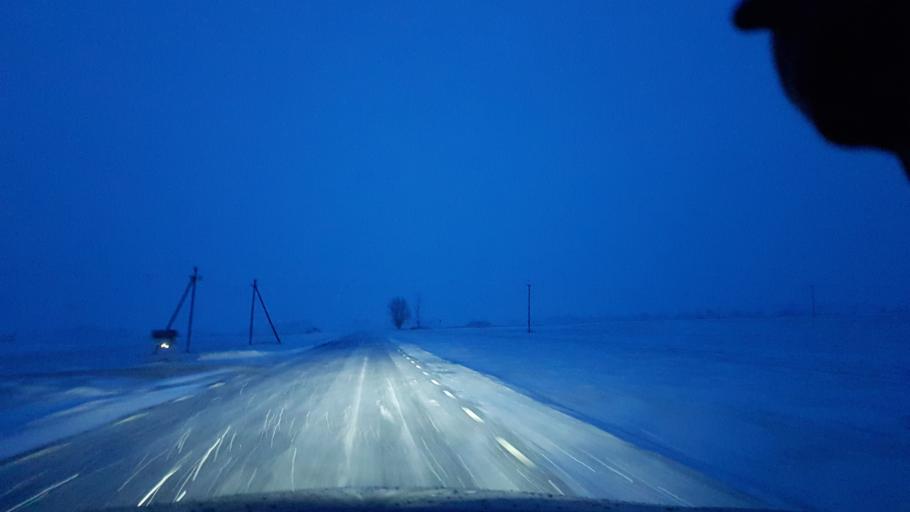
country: EE
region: Laeaene-Virumaa
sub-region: Vaeike-Maarja vald
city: Vaike-Maarja
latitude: 59.0606
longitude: 26.4257
